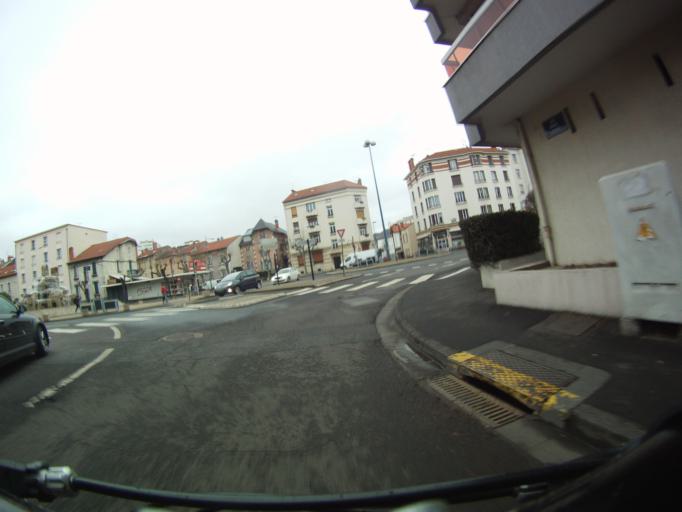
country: FR
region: Auvergne
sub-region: Departement du Puy-de-Dome
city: Clermont-Ferrand
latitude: 45.7742
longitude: 3.0758
